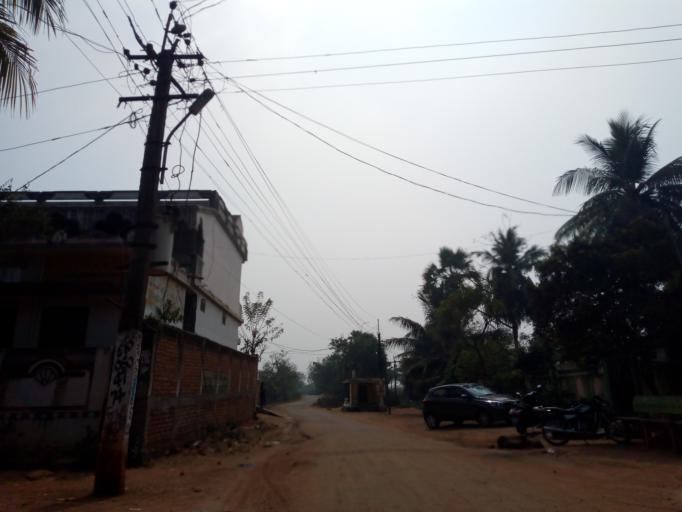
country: IN
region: Andhra Pradesh
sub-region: West Godavari
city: Tadepallegudem
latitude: 16.8716
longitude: 81.3195
